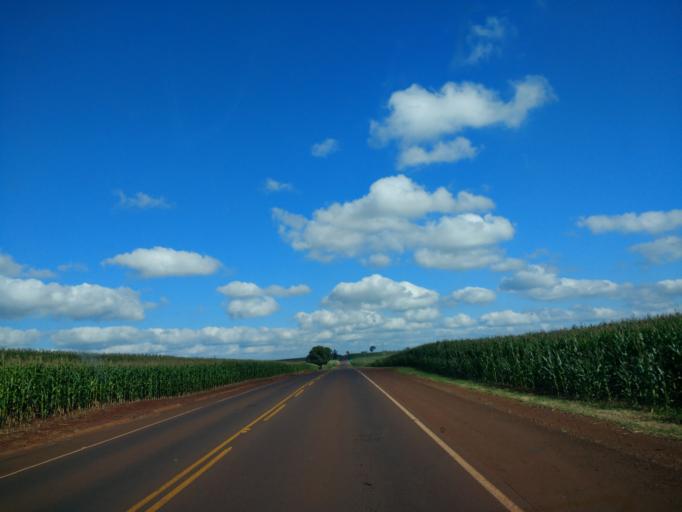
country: BR
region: Parana
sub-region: Palotina
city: Palotina
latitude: -24.3586
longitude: -53.5464
